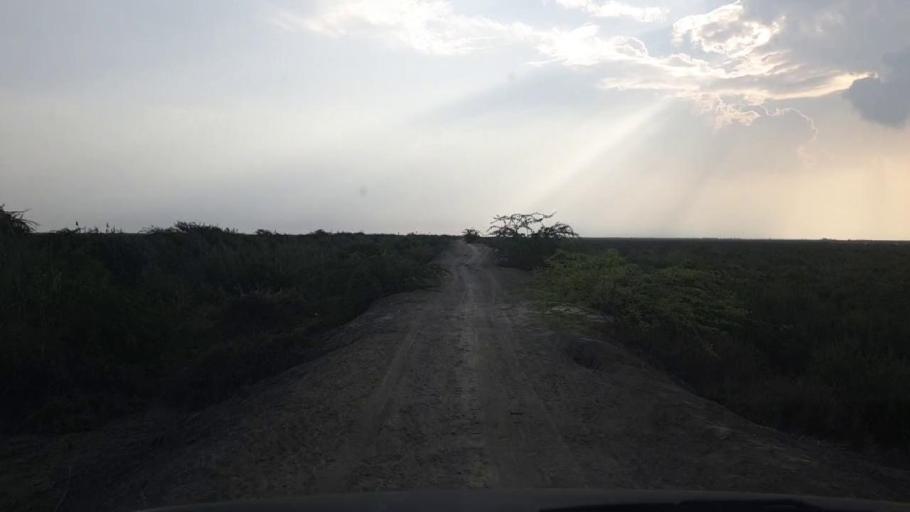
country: PK
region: Sindh
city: Badin
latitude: 24.4552
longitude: 68.6859
